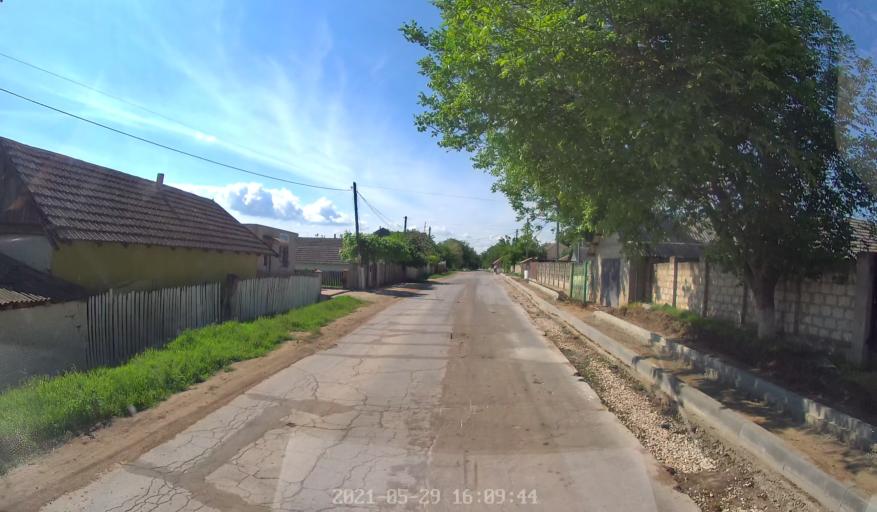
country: MD
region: Chisinau
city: Singera
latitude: 46.8213
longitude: 28.8803
